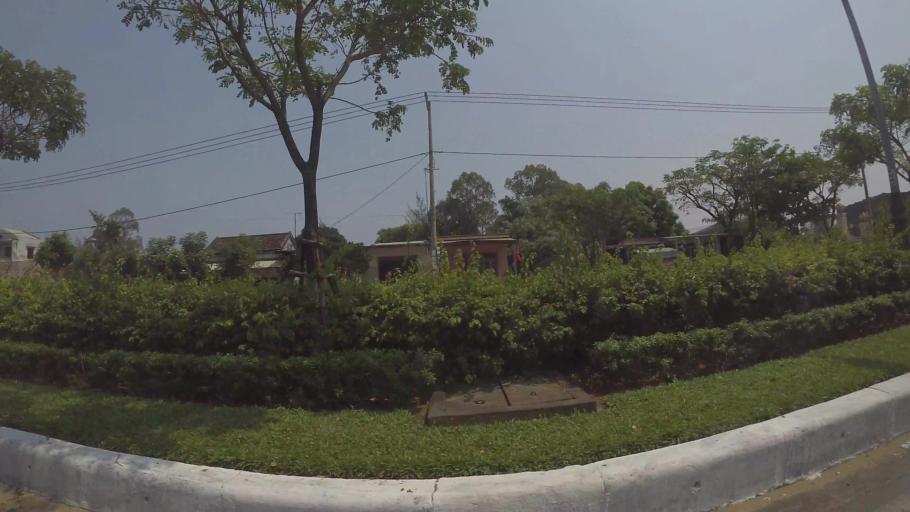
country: VN
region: Da Nang
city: Ngu Hanh Son
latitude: 15.9820
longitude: 108.2558
